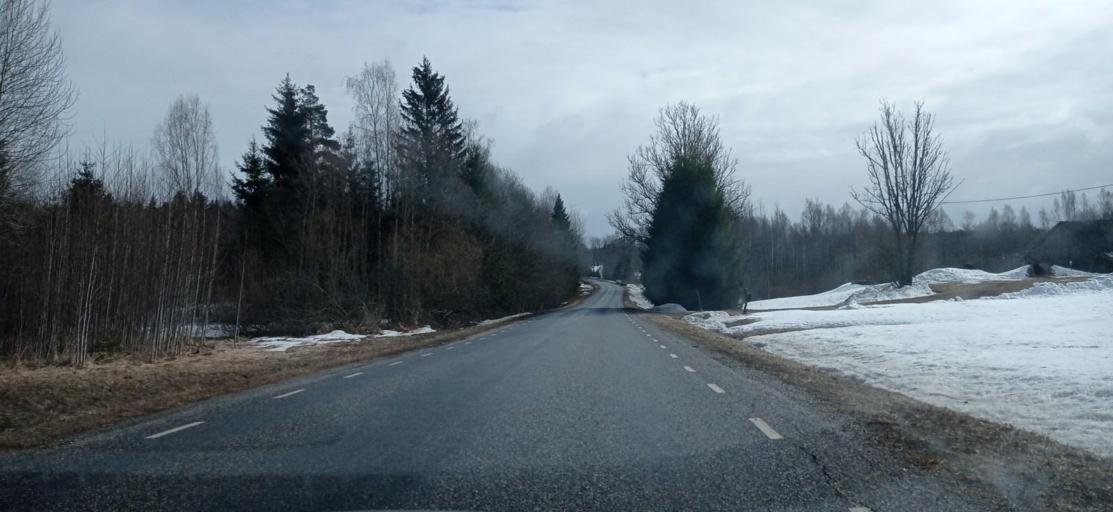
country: EE
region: Tartu
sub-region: UElenurme vald
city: Ulenurme
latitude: 58.0693
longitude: 26.7134
